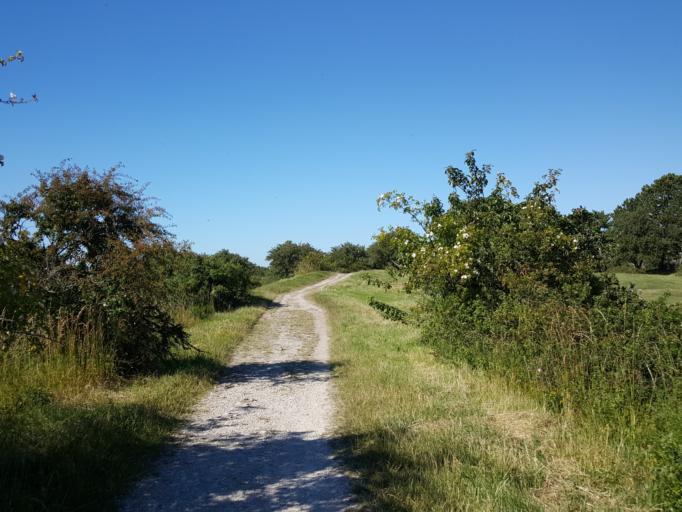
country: SE
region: Gotland
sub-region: Gotland
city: Visby
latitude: 57.6428
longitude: 18.3020
